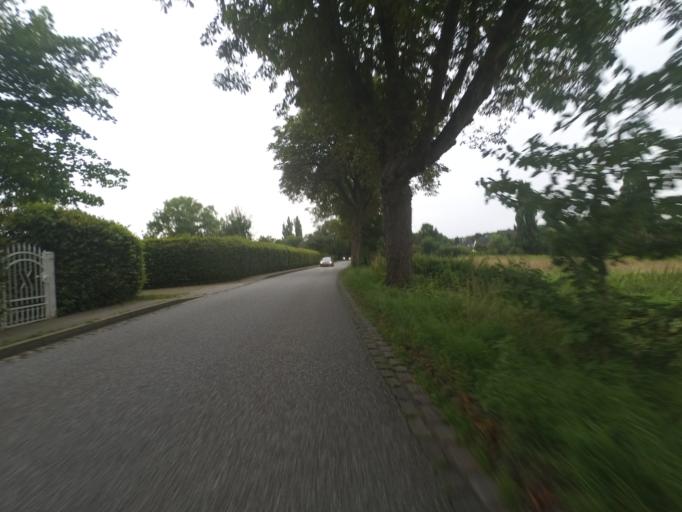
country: DE
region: Schleswig-Holstein
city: Oststeinbek
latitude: 53.4990
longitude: 10.1733
